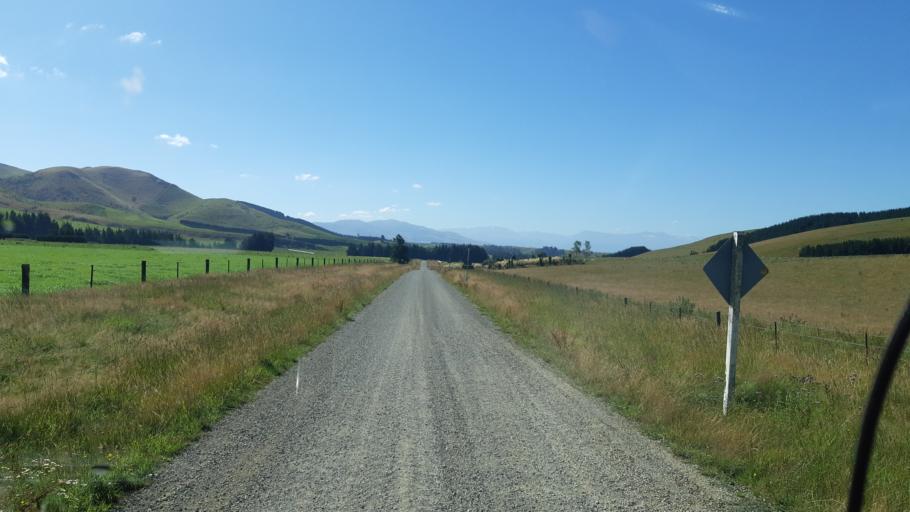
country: NZ
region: Canterbury
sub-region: Timaru District
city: Pleasant Point
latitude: -44.3270
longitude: 170.8629
